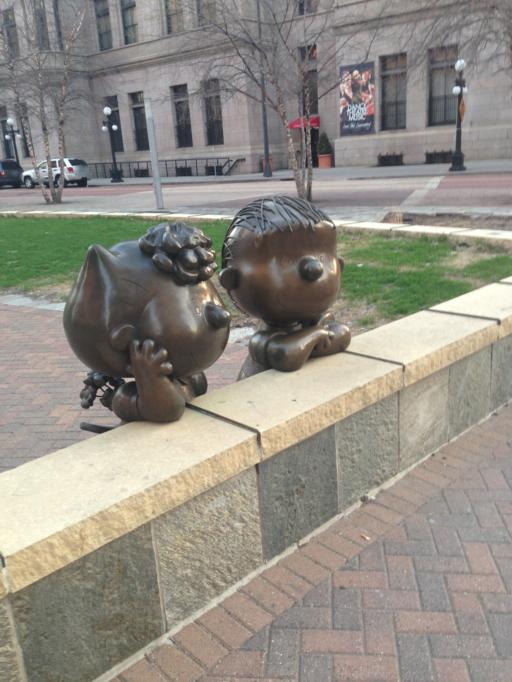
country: US
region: Minnesota
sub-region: Ramsey County
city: Saint Paul
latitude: 44.9460
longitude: -93.0967
